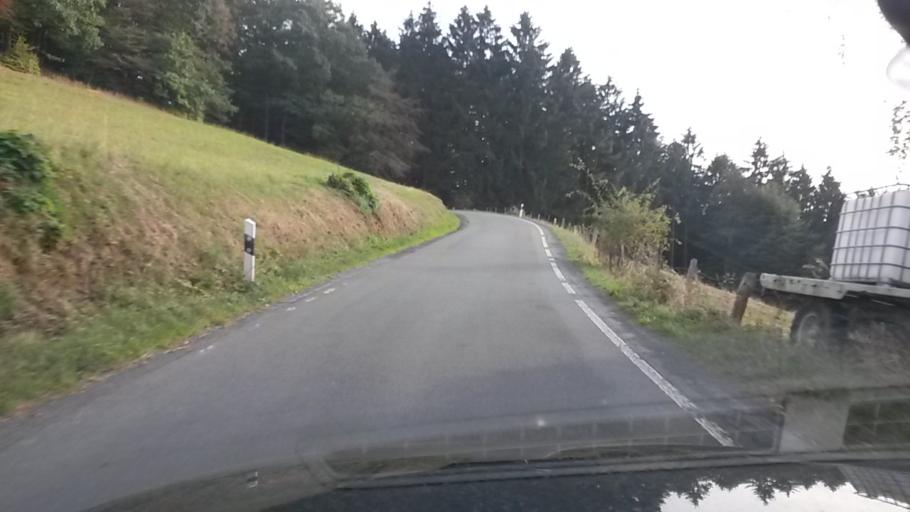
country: DE
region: North Rhine-Westphalia
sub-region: Regierungsbezirk Arnsberg
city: Herscheid
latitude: 51.2110
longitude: 7.7591
